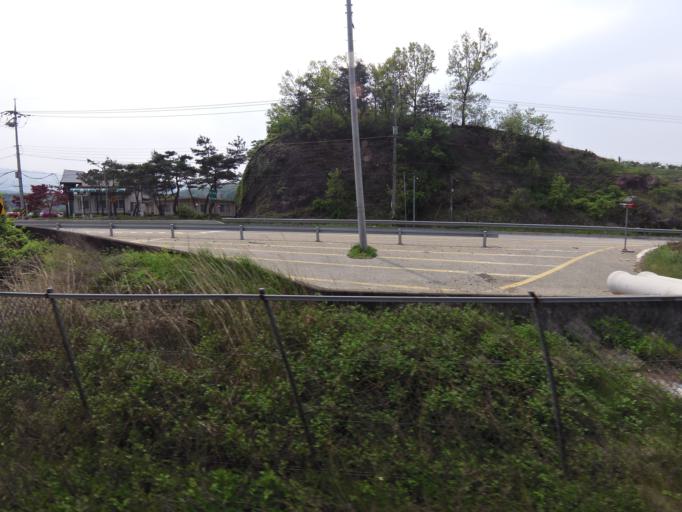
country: KR
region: Chungcheongbuk-do
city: Yong-dong
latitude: 36.1711
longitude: 127.7991
